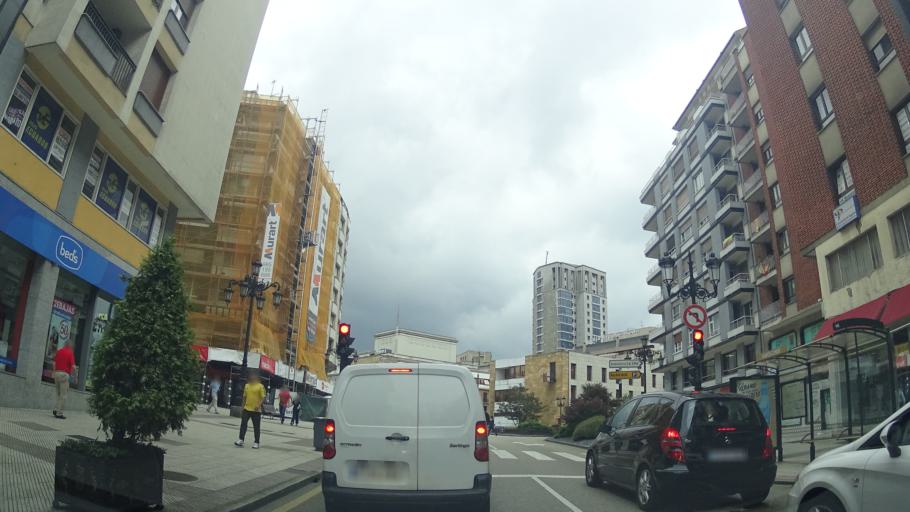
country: ES
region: Asturias
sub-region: Province of Asturias
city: Oviedo
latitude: 43.3640
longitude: -5.8462
